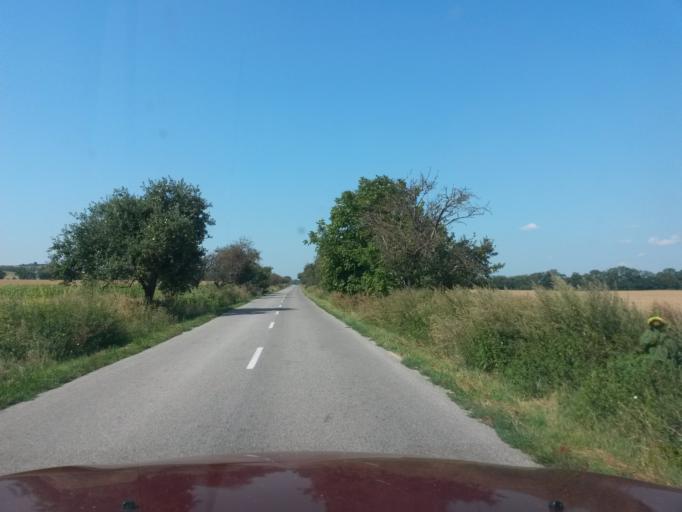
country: HU
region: Borsod-Abauj-Zemplen
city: Gonc
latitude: 48.5343
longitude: 21.1637
